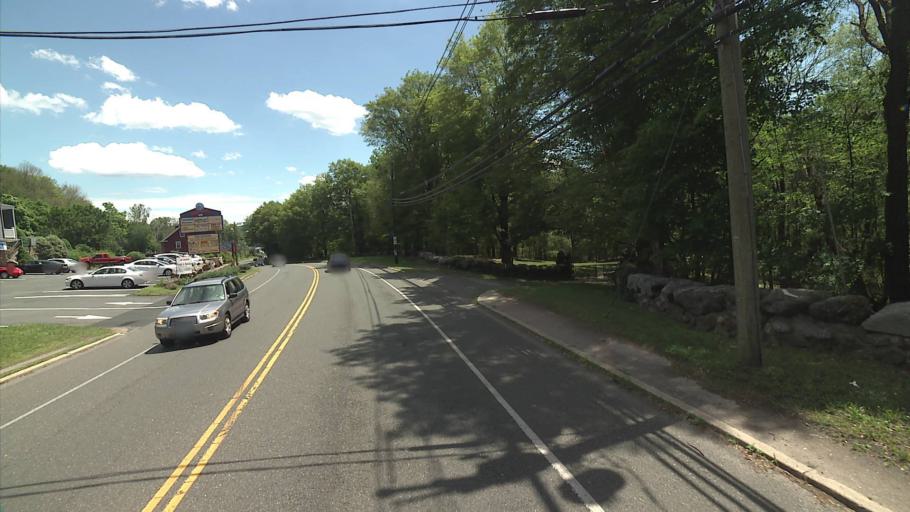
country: US
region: Connecticut
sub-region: New Haven County
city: Naugatuck
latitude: 41.4781
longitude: -73.0474
